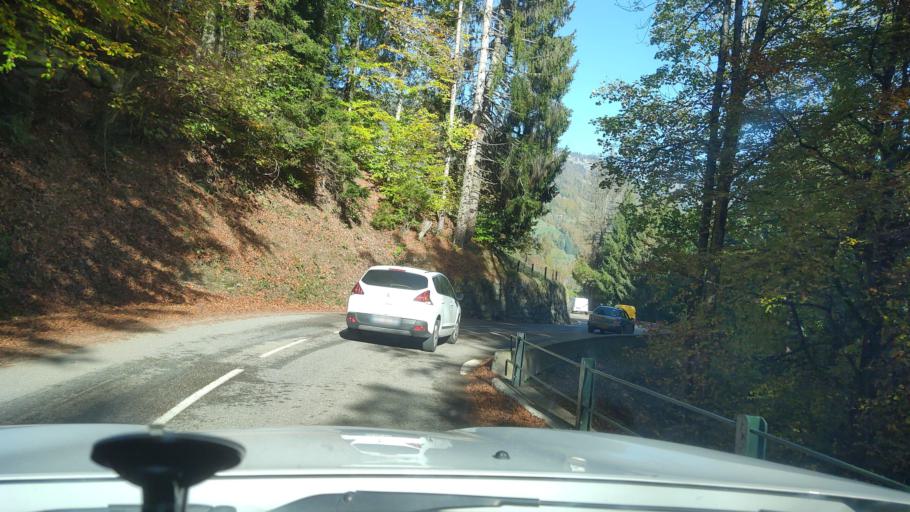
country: FR
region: Rhone-Alpes
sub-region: Departement de la Savoie
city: Ugine
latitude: 45.7840
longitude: 6.4813
